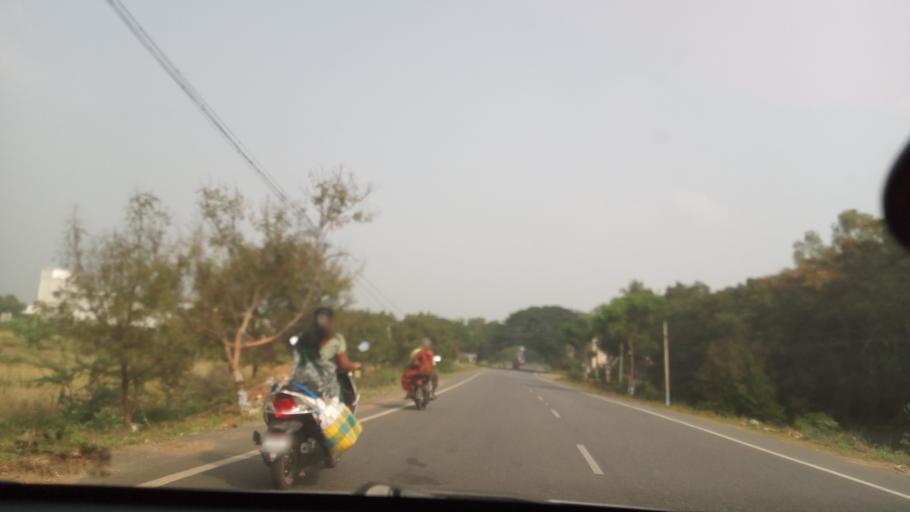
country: IN
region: Tamil Nadu
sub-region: Erode
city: Punjai Puliyampatti
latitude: 11.3663
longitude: 77.1714
